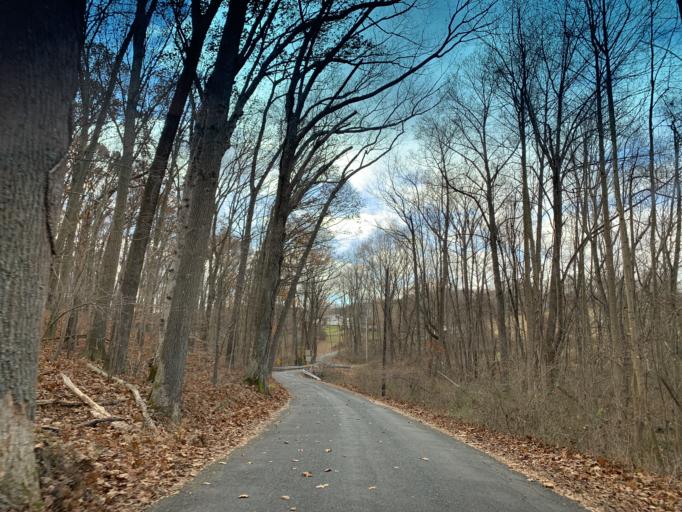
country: US
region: Maryland
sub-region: Harford County
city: Bel Air North
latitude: 39.5928
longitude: -76.4117
